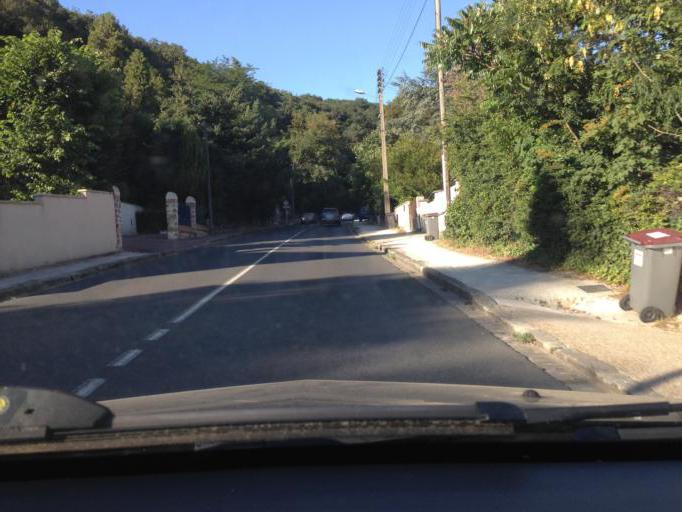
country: FR
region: Ile-de-France
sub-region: Departement des Yvelines
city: Saint-Remy-les-Chevreuse
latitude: 48.7079
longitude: 2.0760
